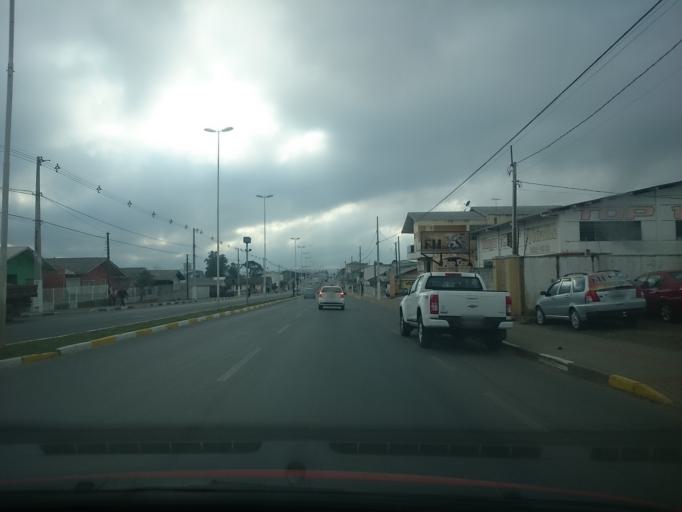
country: BR
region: Santa Catarina
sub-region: Lages
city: Lages
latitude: -27.8316
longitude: -50.3452
